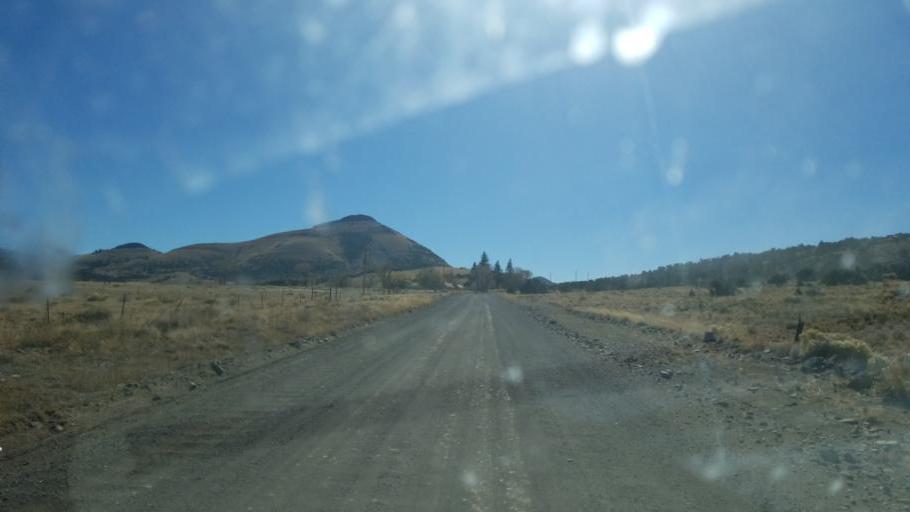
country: US
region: Colorado
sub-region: Rio Grande County
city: Del Norte
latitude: 37.6303
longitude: -106.3635
